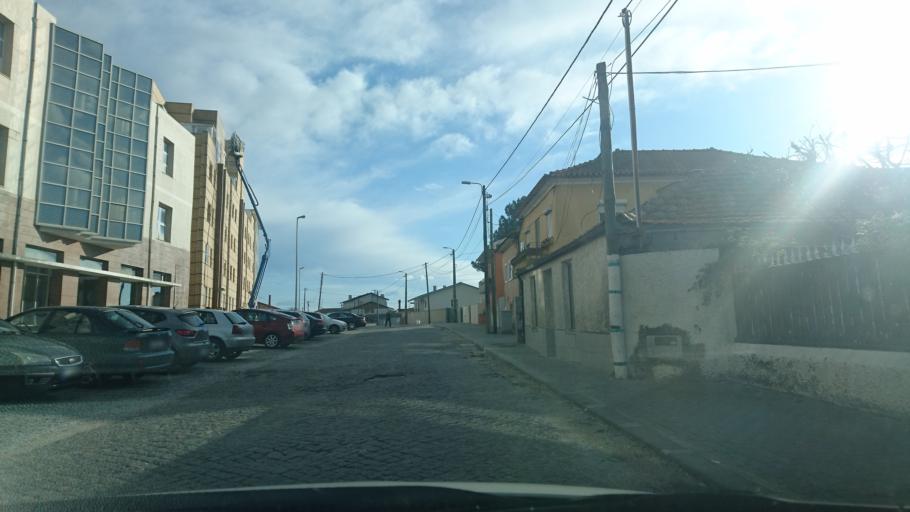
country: PT
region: Aveiro
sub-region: Santa Maria da Feira
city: Pacos de Brandao
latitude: 40.9731
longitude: -8.5792
